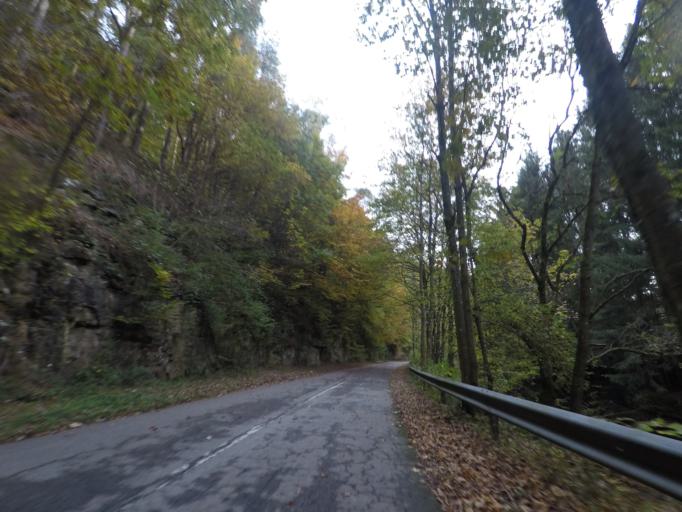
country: LU
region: Luxembourg
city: Itzig
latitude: 49.5965
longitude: 6.1612
